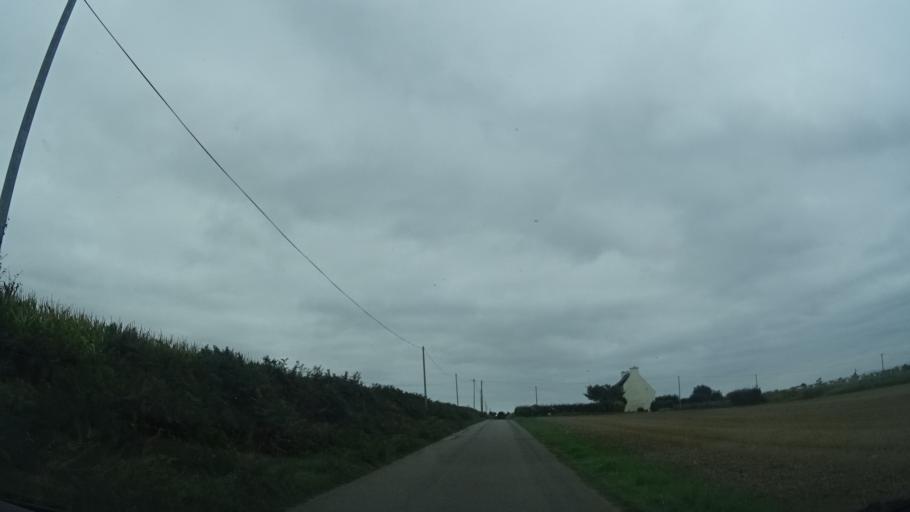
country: FR
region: Brittany
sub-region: Departement du Finistere
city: Lampaul-Plouarzel
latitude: 48.4555
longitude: -4.7557
